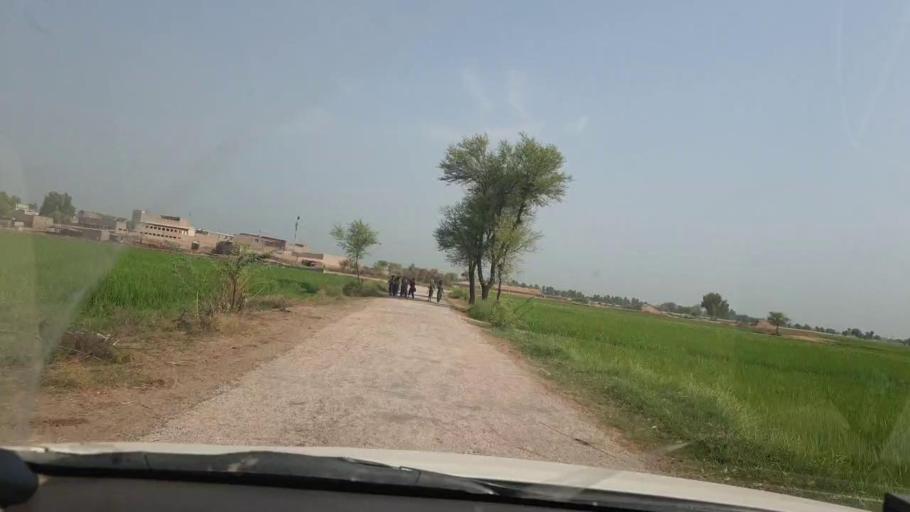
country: PK
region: Sindh
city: Chak
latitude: 27.8365
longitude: 68.7986
